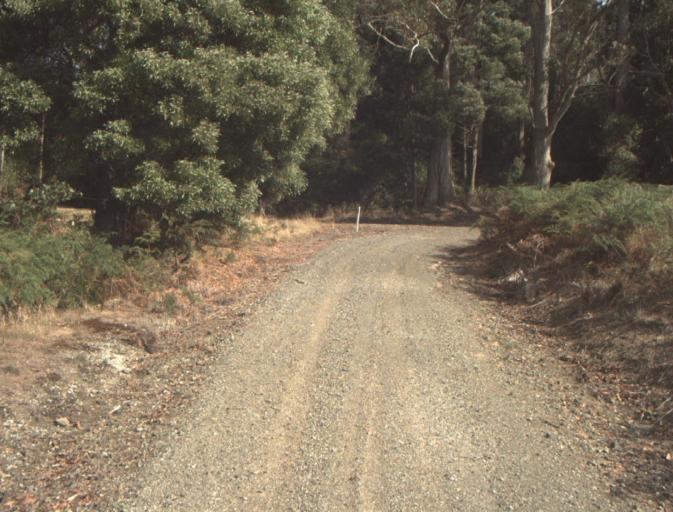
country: AU
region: Tasmania
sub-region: Launceston
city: Mayfield
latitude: -41.1834
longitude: 147.1937
